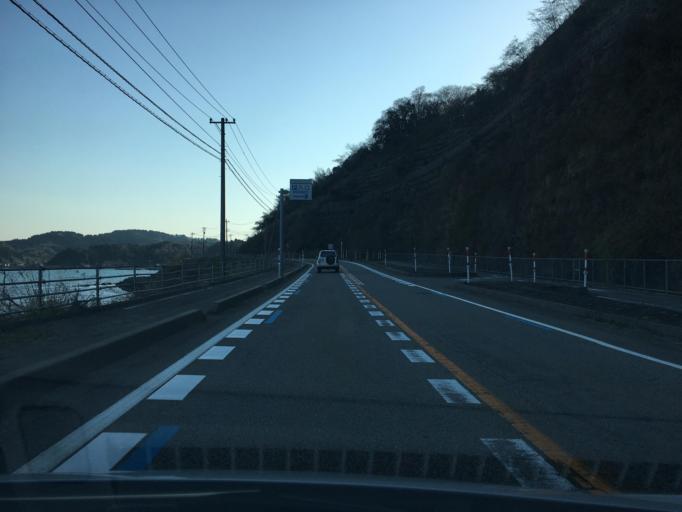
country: JP
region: Toyama
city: Himi
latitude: 36.9454
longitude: 137.0343
